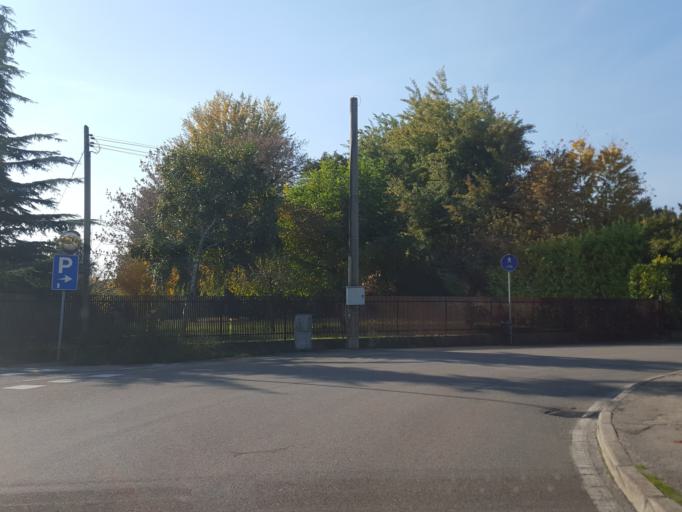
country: IT
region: Veneto
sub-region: Provincia di Verona
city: San Bonifacio
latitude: 45.3908
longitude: 11.2746
